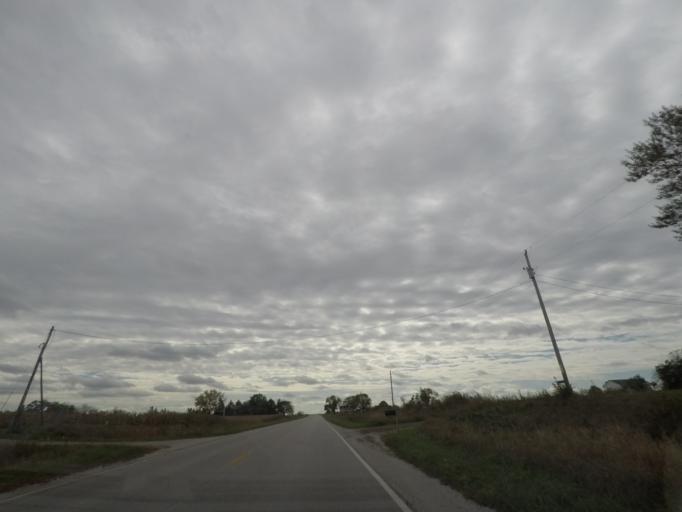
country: US
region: Iowa
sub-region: Story County
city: Huxley
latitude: 41.8656
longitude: -93.5316
